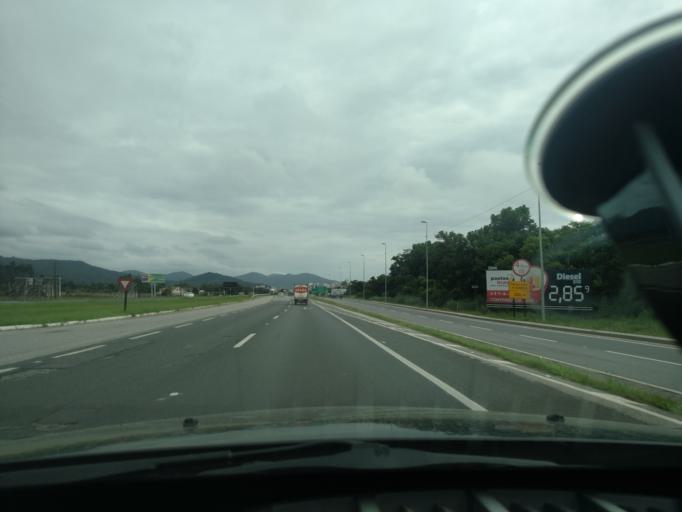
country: BR
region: Santa Catarina
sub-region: Itapema
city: Itapema
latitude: -27.1449
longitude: -48.6103
